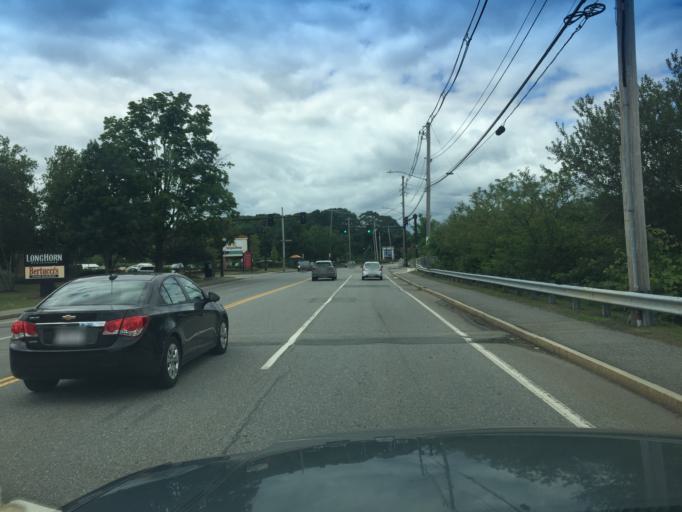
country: US
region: Massachusetts
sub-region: Middlesex County
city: Reading
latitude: 42.5191
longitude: -71.0938
